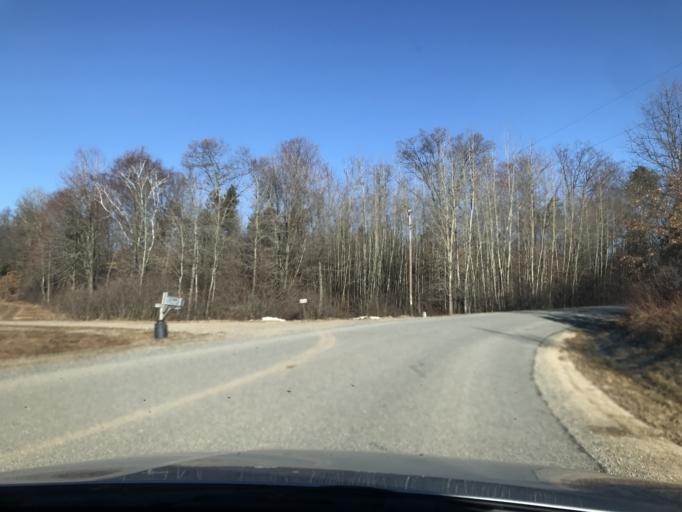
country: US
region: Wisconsin
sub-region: Marinette County
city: Niagara
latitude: 45.3809
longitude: -88.0388
